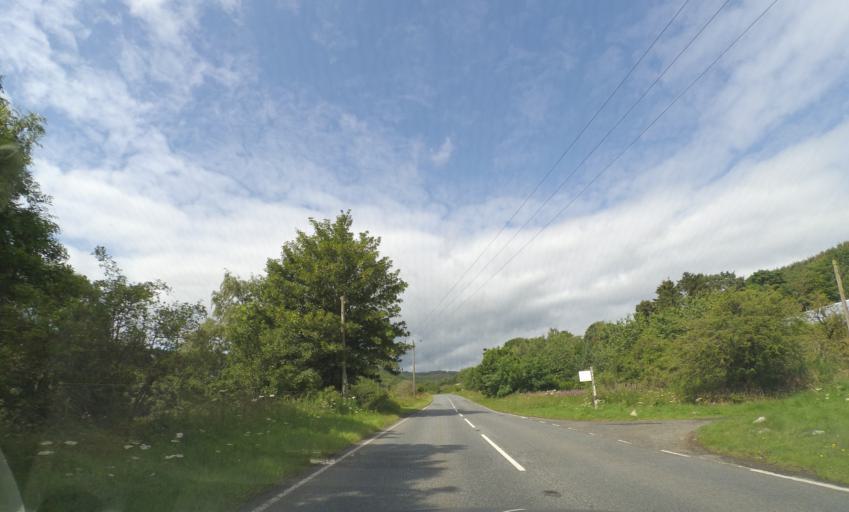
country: GB
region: Scotland
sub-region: The Scottish Borders
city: Selkirk
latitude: 55.6169
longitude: -2.9301
